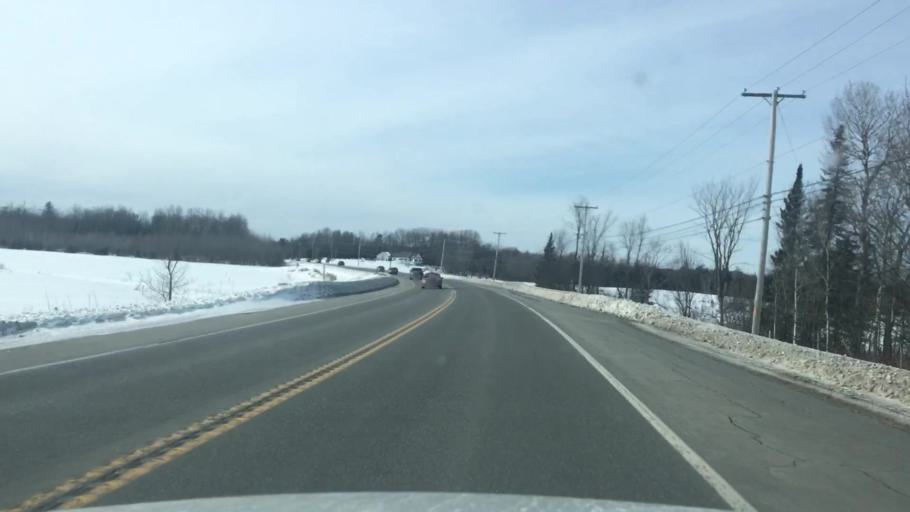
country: US
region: Maine
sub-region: Penobscot County
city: Kenduskeag
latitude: 44.9102
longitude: -68.8978
